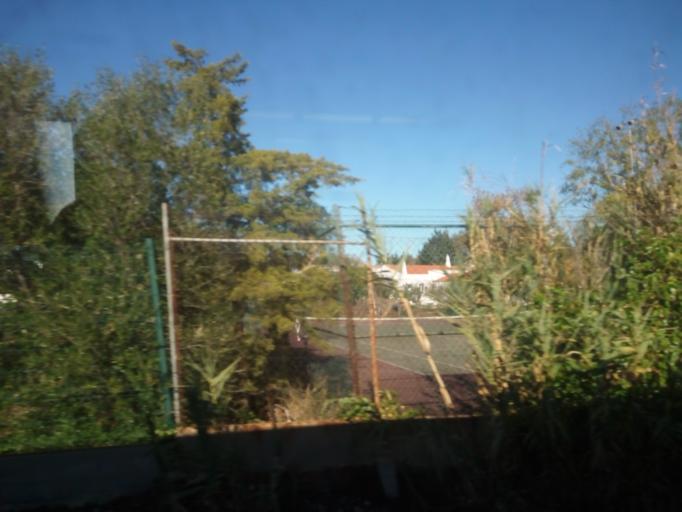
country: PT
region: Faro
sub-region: Loule
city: Almancil
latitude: 37.1034
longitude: -8.0536
